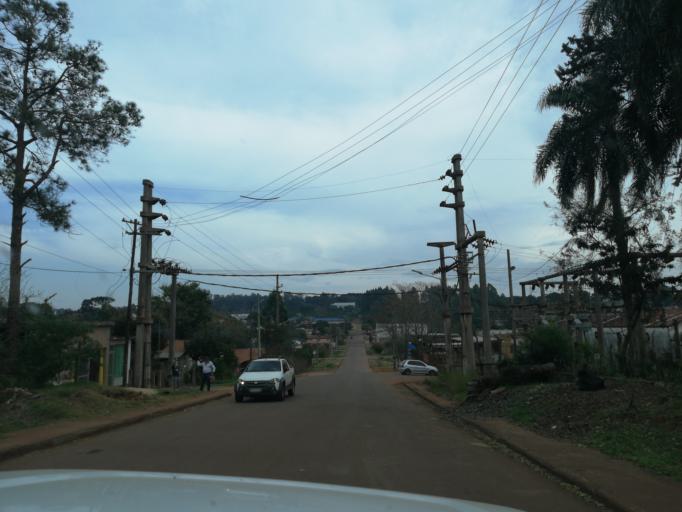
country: AR
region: Misiones
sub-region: Departamento de San Pedro
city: San Pedro
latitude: -26.6251
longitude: -54.1096
